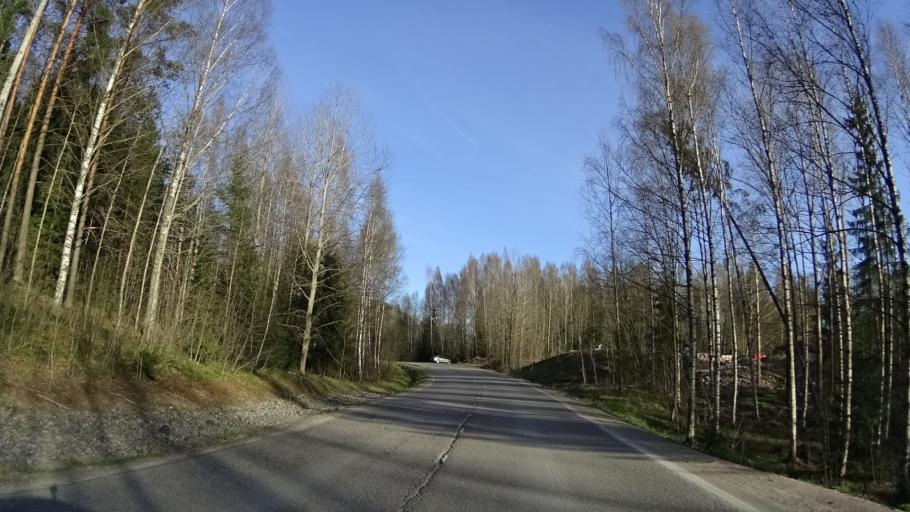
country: FI
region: Uusimaa
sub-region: Helsinki
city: Kilo
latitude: 60.2942
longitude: 24.7979
